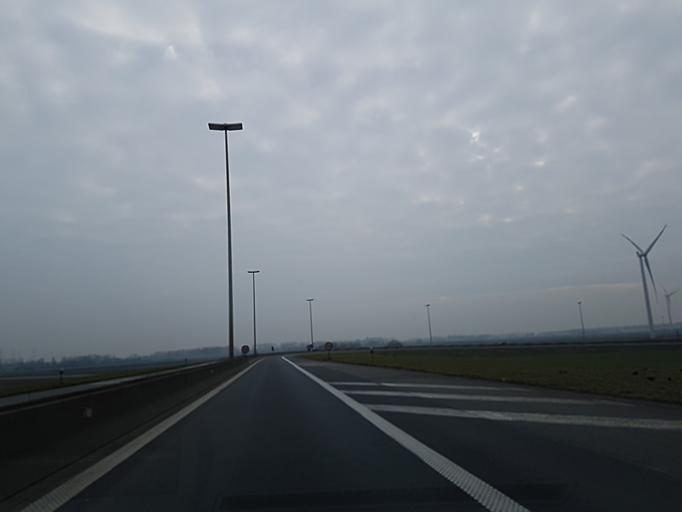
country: BE
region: Flanders
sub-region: Provincie Oost-Vlaanderen
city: Beveren
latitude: 51.2418
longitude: 4.2452
